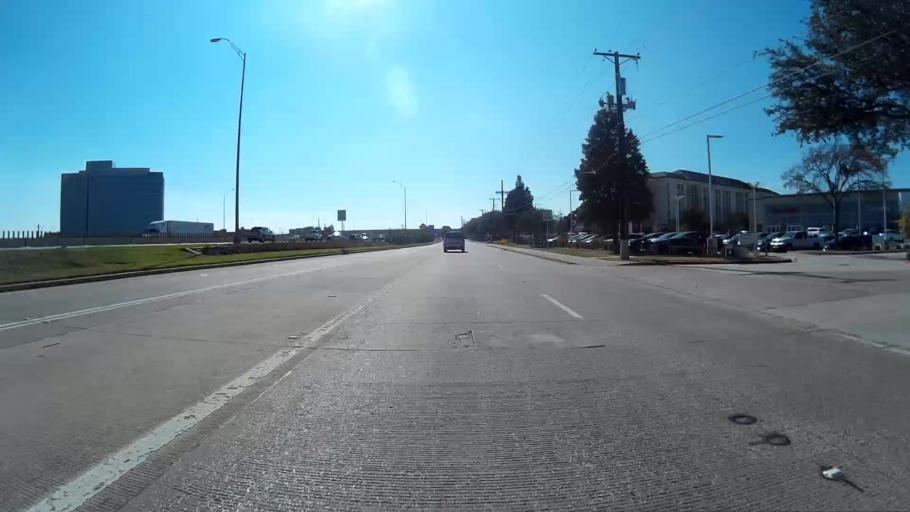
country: US
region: Texas
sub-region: Dallas County
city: Richardson
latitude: 32.9718
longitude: -96.7189
